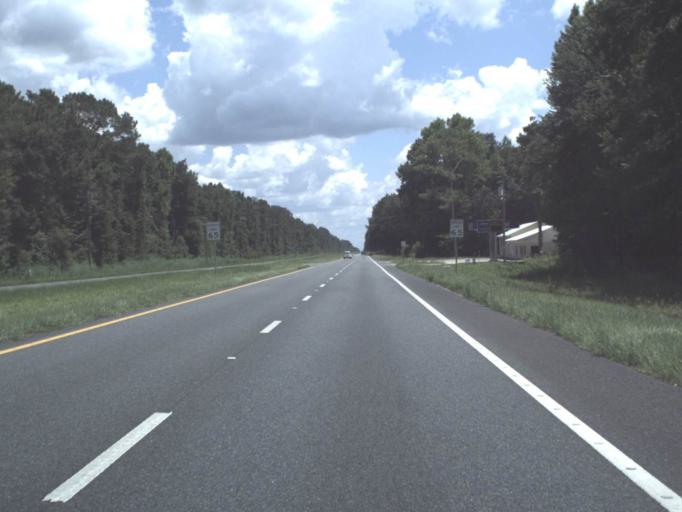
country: US
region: Florida
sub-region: Taylor County
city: Perry
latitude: 30.3011
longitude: -83.7463
